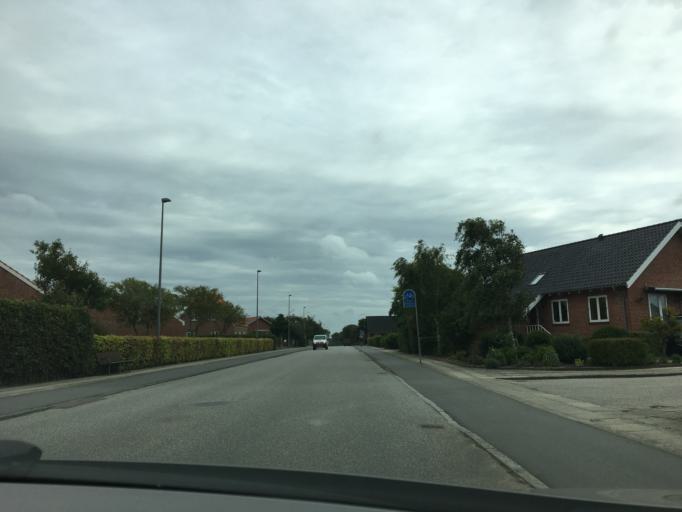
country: DK
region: Central Jutland
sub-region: Ringkobing-Skjern Kommune
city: Ringkobing
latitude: 56.0841
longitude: 8.2550
